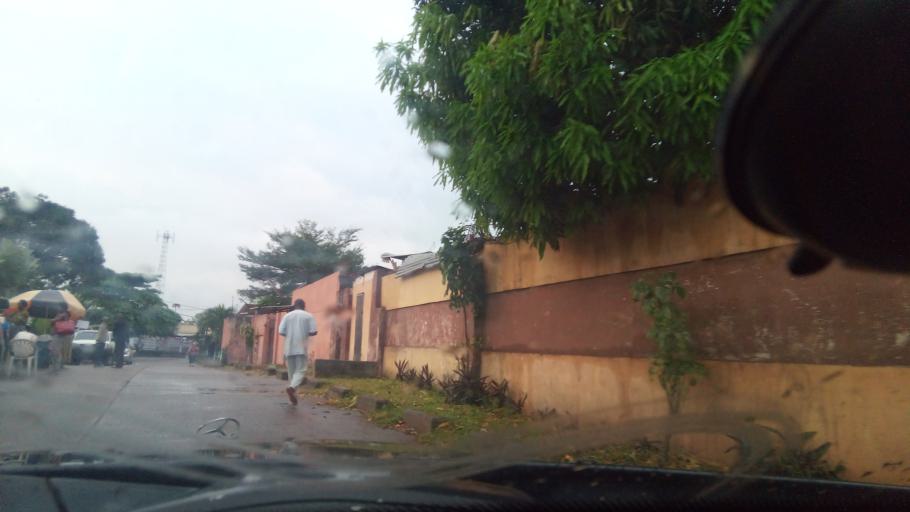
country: CD
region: Kinshasa
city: Kinshasa
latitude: -4.3452
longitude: 15.2407
